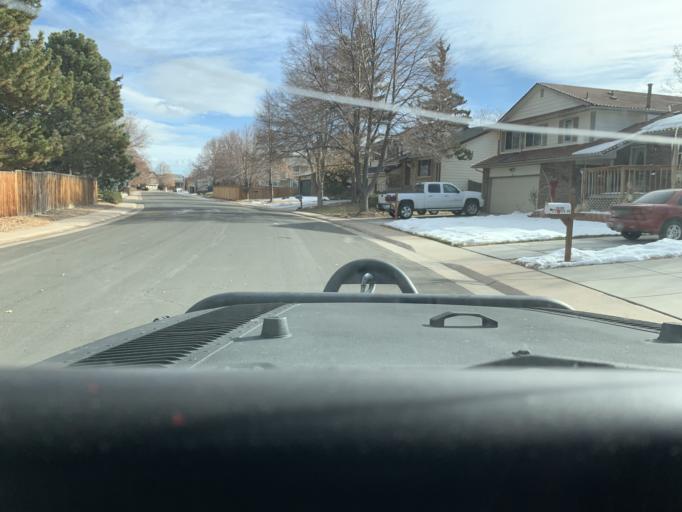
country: US
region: Colorado
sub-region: Adams County
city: Aurora
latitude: 39.7054
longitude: -104.7987
